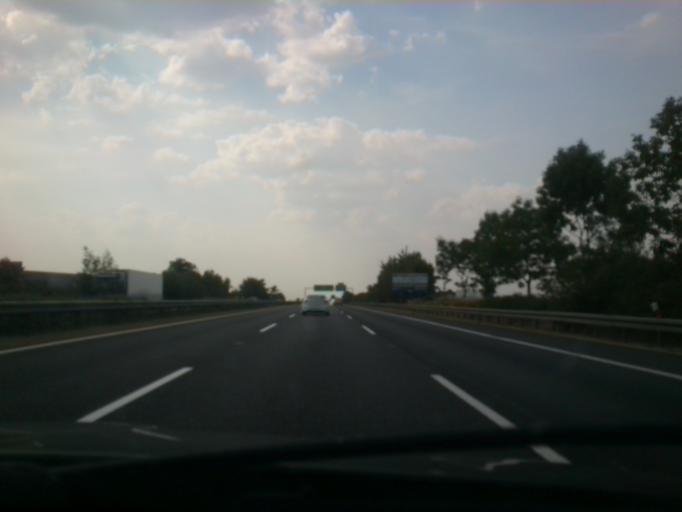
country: CZ
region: Central Bohemia
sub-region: Okres Praha-Vychod
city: Strancice
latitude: 49.9429
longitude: 14.6630
